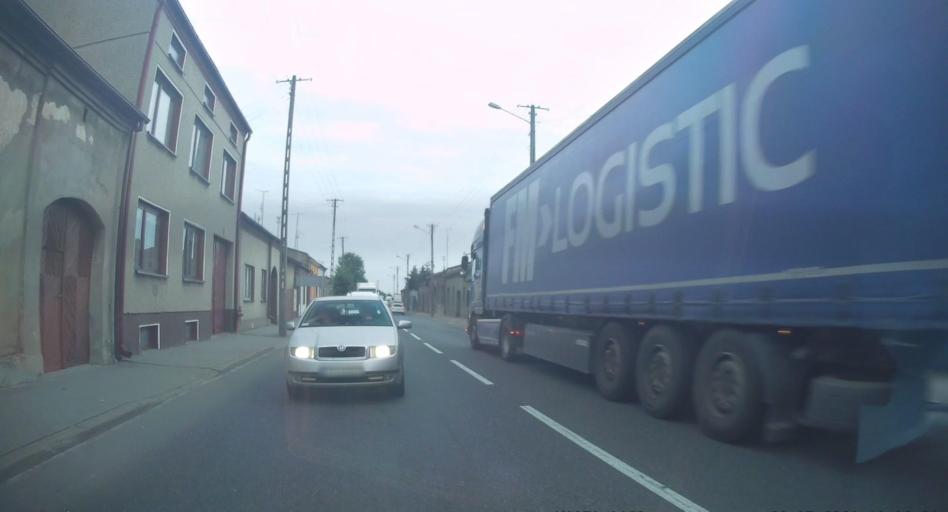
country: PL
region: Lodz Voivodeship
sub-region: Powiat radomszczanski
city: Kamiensk
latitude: 51.2027
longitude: 19.4984
